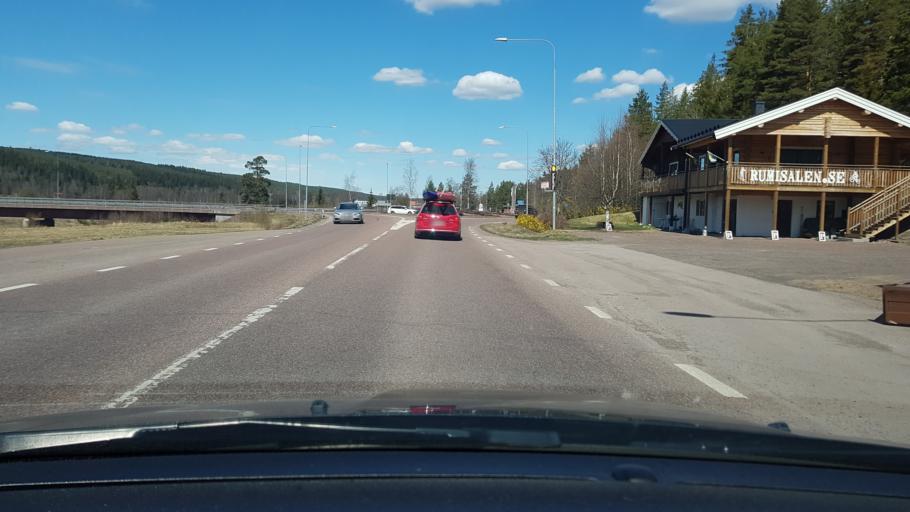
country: SE
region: Dalarna
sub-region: Malung-Saelens kommun
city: Malung
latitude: 61.1482
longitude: 13.2739
